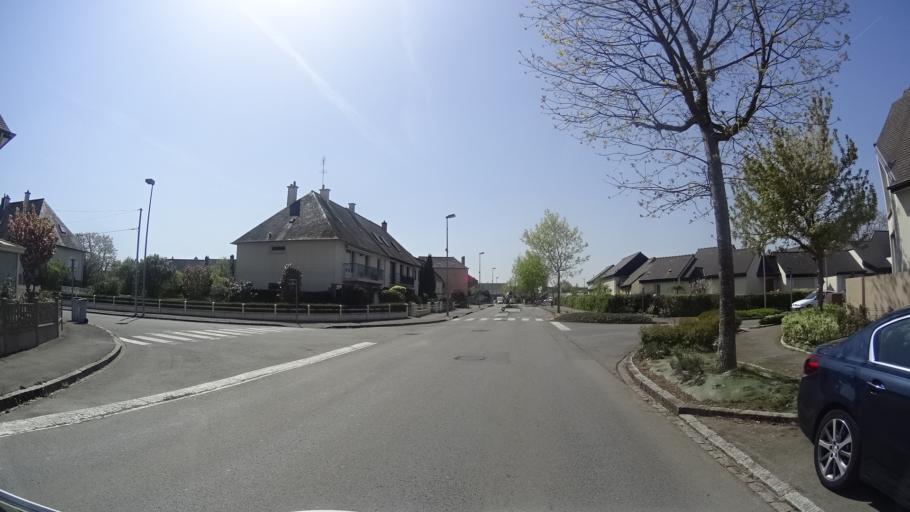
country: FR
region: Brittany
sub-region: Departement d'Ille-et-Vilaine
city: Chavagne
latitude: 48.0556
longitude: -1.7896
